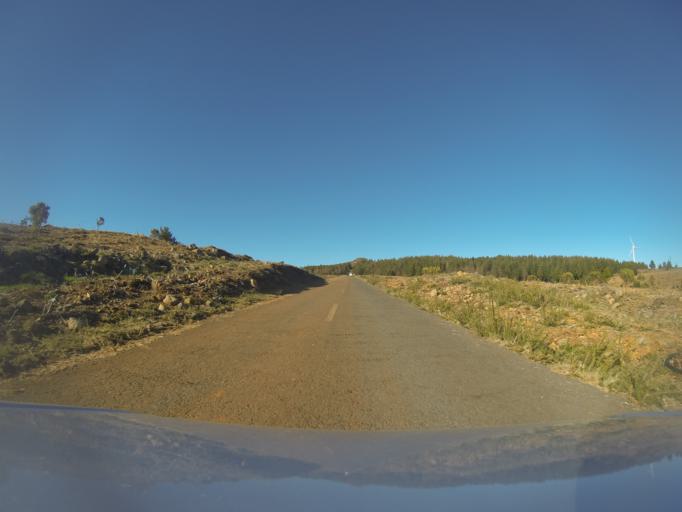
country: PT
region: Madeira
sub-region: Sao Vicente
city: Sao Vicente
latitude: 32.7701
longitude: -17.0785
